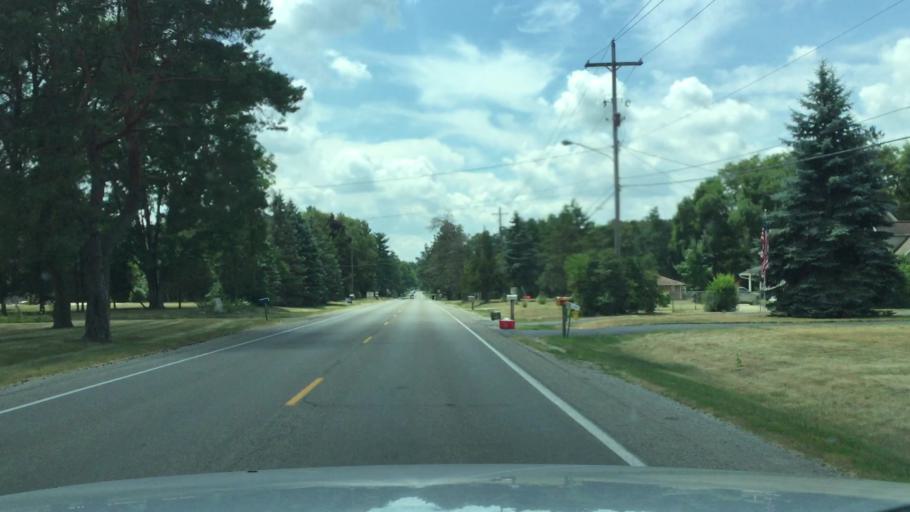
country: US
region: Michigan
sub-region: Genesee County
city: Flushing
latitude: 43.0812
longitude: -83.8690
